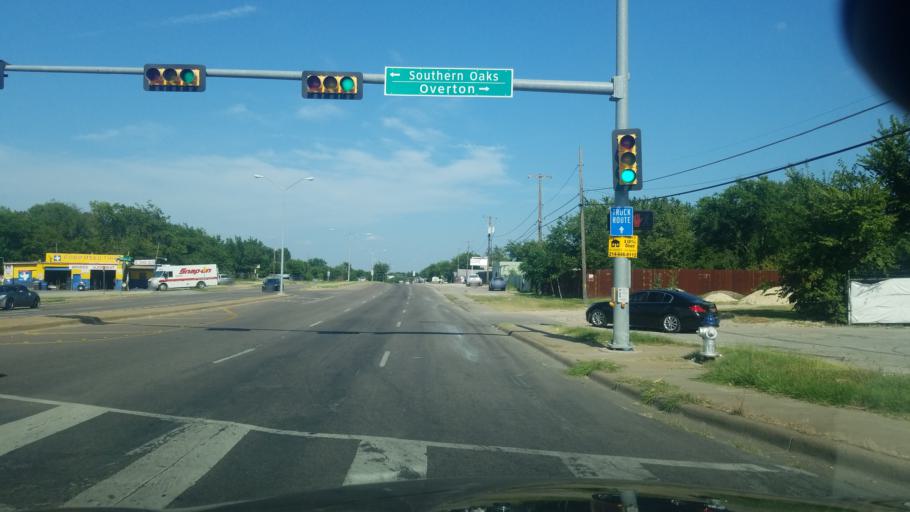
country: US
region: Texas
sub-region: Dallas County
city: Dallas
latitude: 32.7161
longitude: -96.7744
